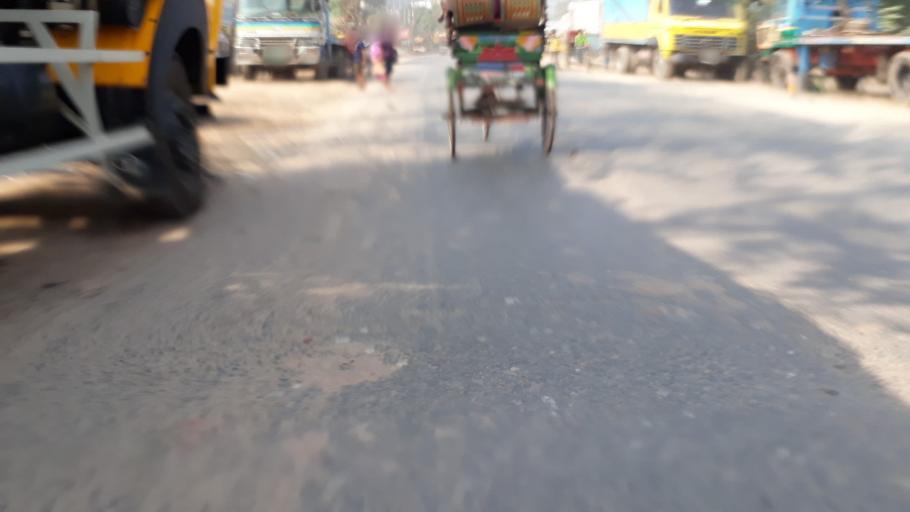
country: BD
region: Dhaka
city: Tungi
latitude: 23.8990
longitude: 90.3289
